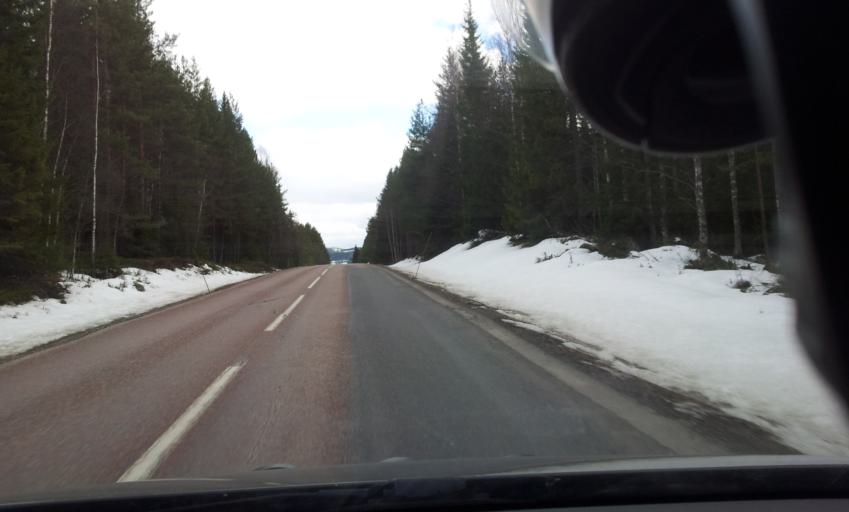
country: SE
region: Gaevleborg
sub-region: Ljusdals Kommun
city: Farila
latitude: 62.1438
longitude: 15.6862
